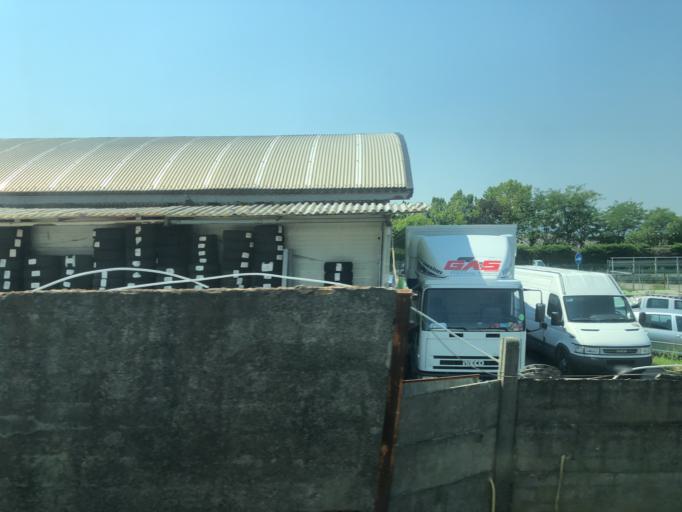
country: IT
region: Emilia-Romagna
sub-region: Provincia di Rimini
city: Santa Giustina
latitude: 44.0707
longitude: 12.5172
